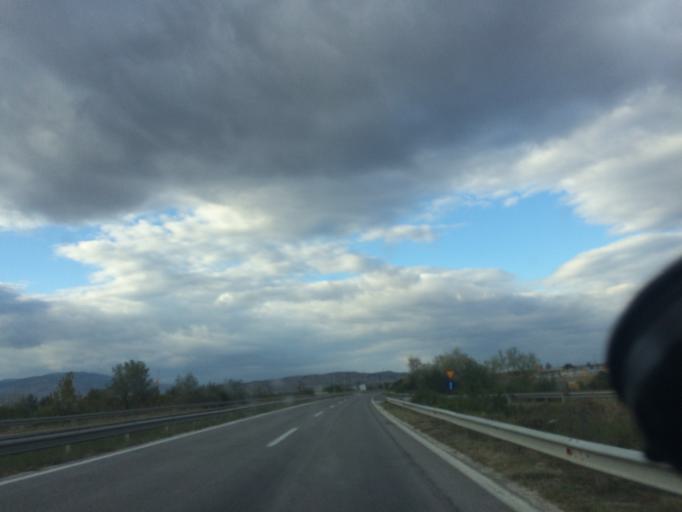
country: MK
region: Petrovec
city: Petrovec
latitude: 41.9535
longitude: 21.6309
